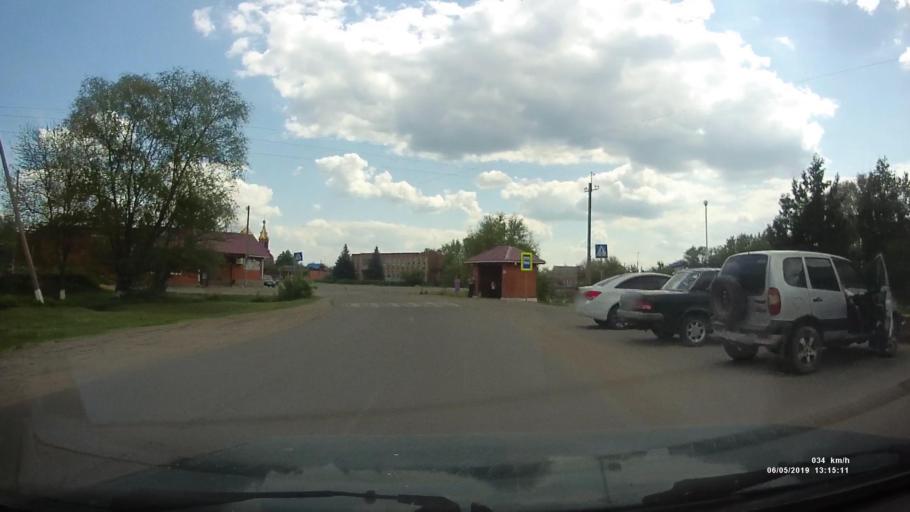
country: RU
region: Rostov
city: Ust'-Donetskiy
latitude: 47.7465
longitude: 40.9444
